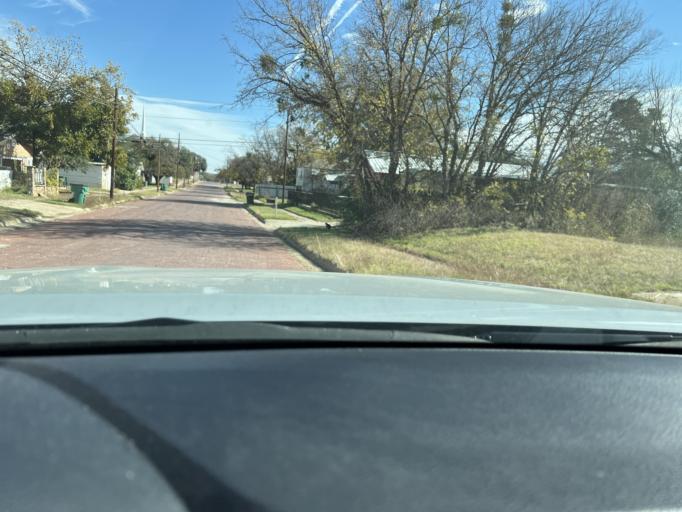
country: US
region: Texas
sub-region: Eastland County
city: Eastland
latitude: 32.3995
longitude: -98.8242
